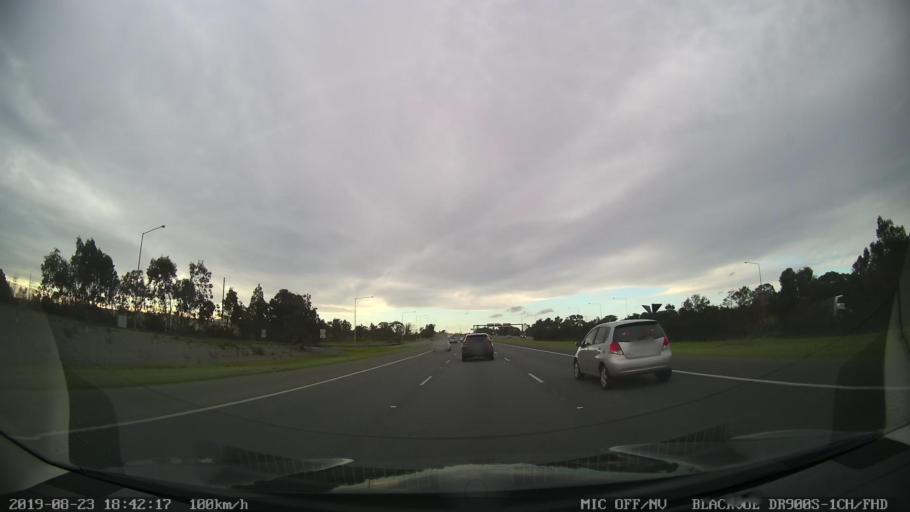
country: AU
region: Victoria
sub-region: Greater Dandenong
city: Keysborough
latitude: -37.9998
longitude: 145.1903
